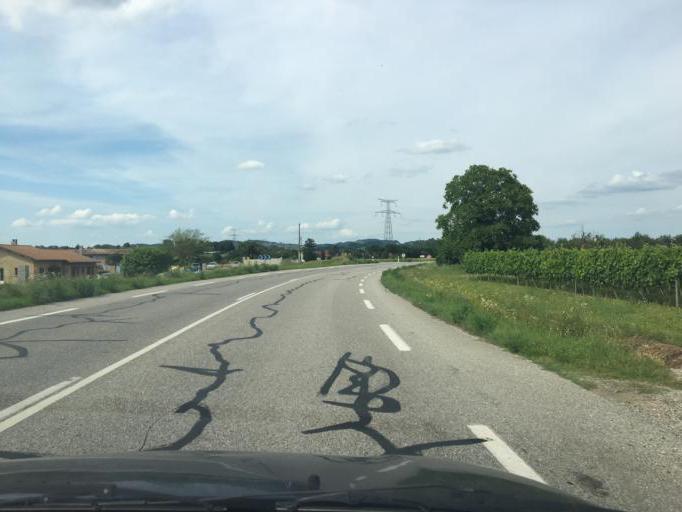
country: FR
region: Rhone-Alpes
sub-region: Departement de la Drome
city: Clerieux
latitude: 45.0923
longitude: 4.9367
